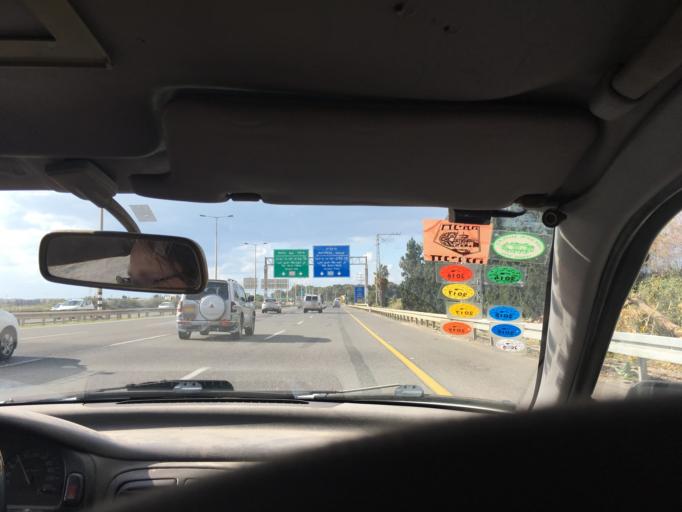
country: IL
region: Tel Aviv
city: Ramat HaSharon
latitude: 32.1378
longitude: 34.8248
